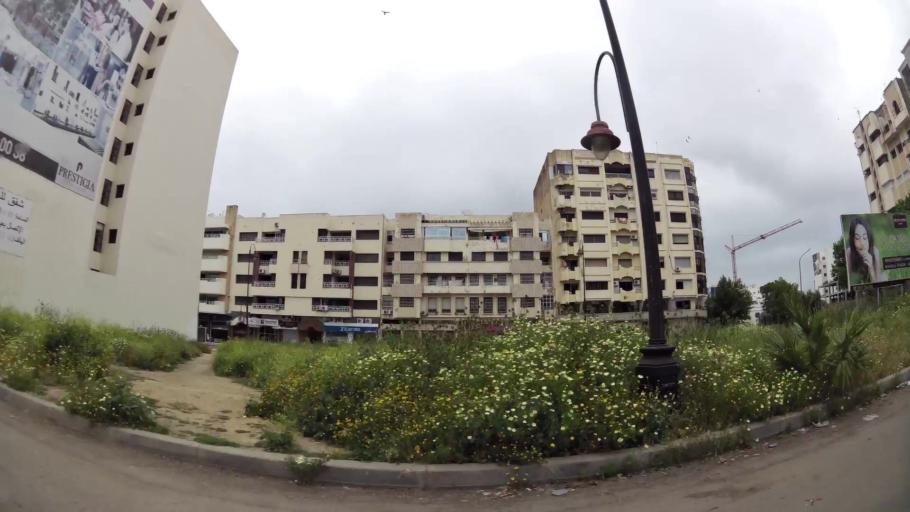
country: MA
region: Fes-Boulemane
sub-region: Fes
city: Fes
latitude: 34.0377
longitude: -5.0082
